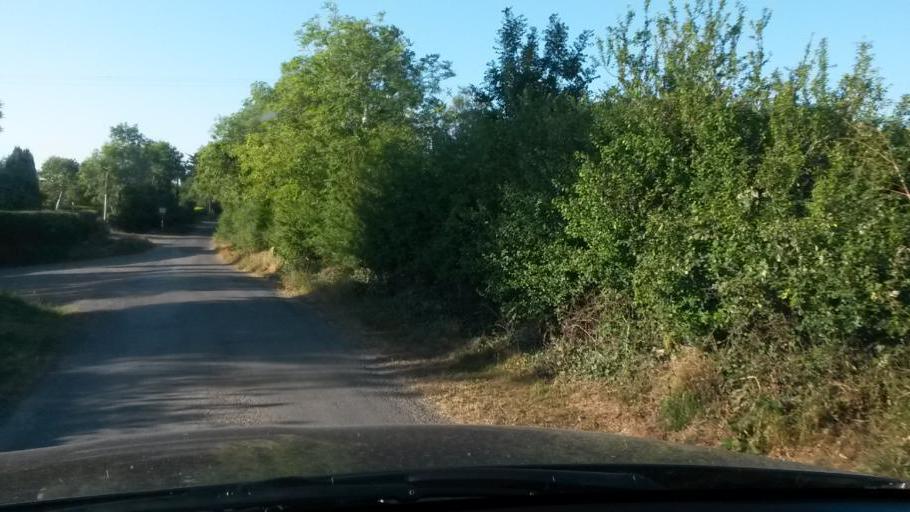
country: IE
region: Leinster
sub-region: Fingal County
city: Swords
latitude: 53.5076
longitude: -6.2939
